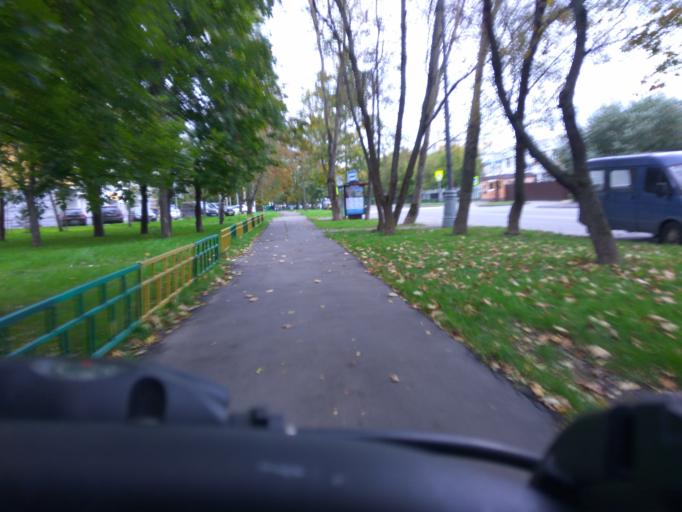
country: RU
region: Moscow
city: Kozeyevo
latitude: 55.8792
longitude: 37.6197
